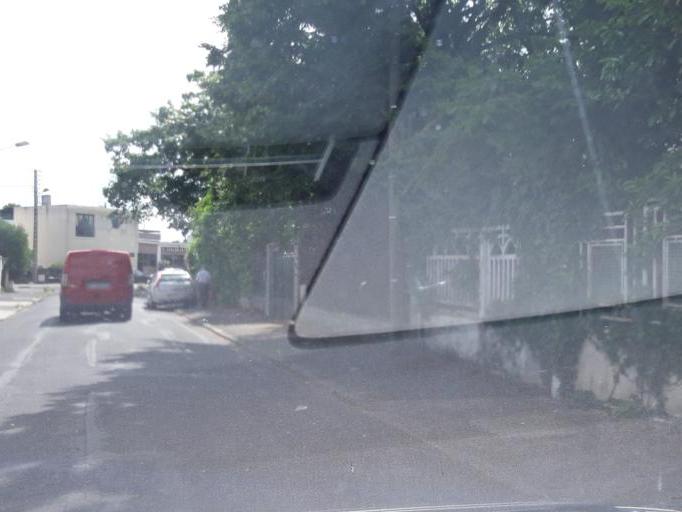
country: FR
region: Ile-de-France
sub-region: Departement de l'Essonne
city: Sainte-Genevieve-des-Bois
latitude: 48.6410
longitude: 2.3318
